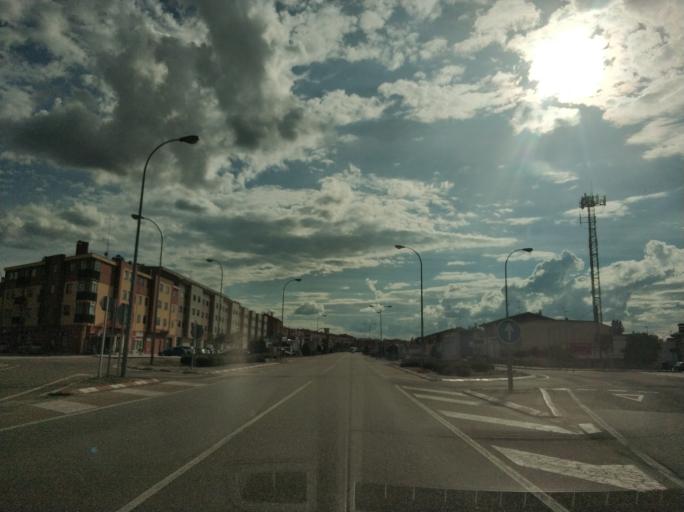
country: ES
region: Castille and Leon
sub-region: Provincia de Valladolid
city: Penafiel
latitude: 41.5998
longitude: -4.1210
